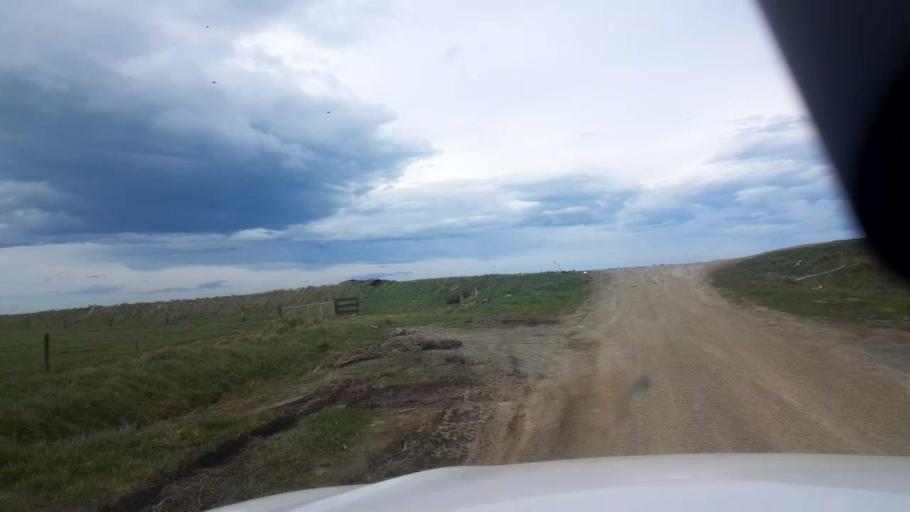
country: NZ
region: Canterbury
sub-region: Timaru District
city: Timaru
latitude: -44.3063
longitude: 171.3156
